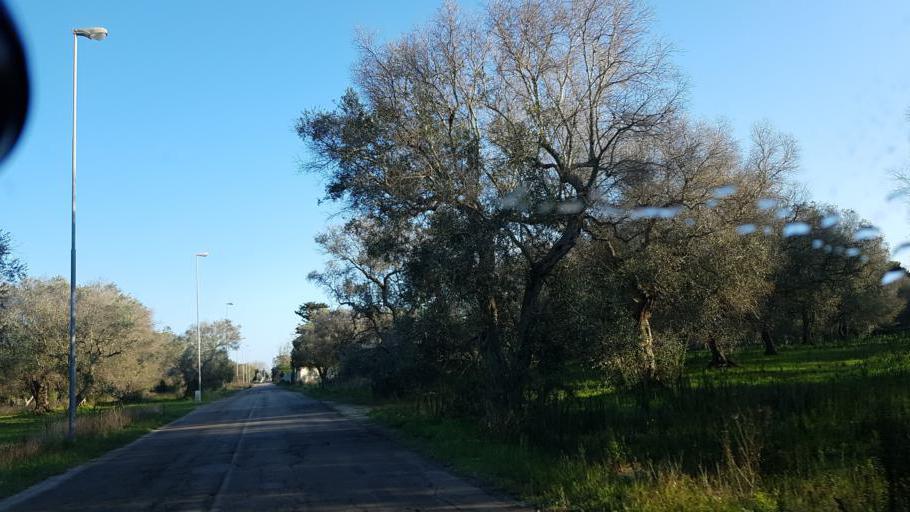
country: IT
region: Apulia
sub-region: Provincia di Brindisi
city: Torchiarolo
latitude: 40.5046
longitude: 18.1038
